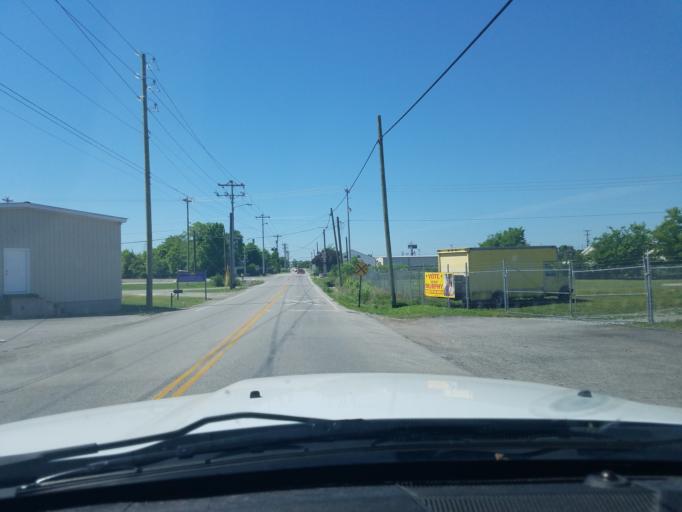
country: US
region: Tennessee
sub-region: Wilson County
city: Lebanon
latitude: 36.2025
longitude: -86.2906
